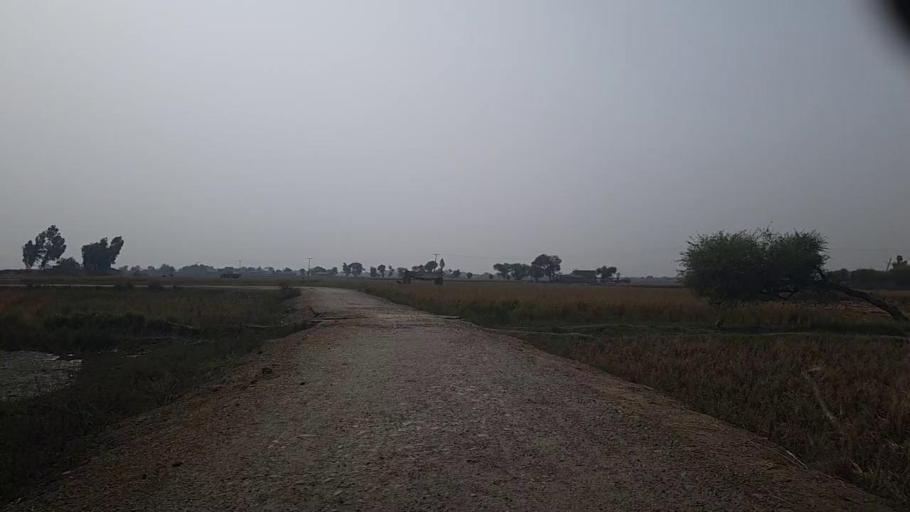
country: PK
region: Sindh
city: Kashmor
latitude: 28.3929
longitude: 69.4221
